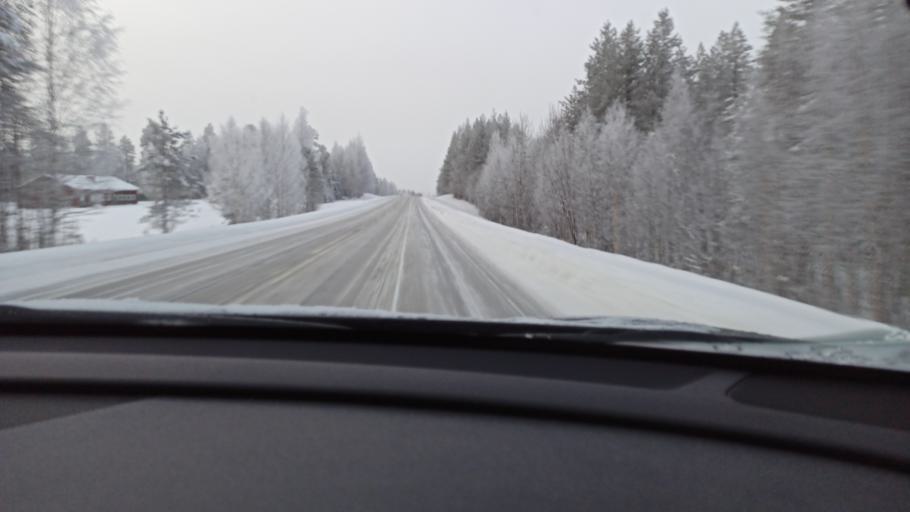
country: FI
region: Lapland
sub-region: Pohjois-Lappi
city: Sodankylae
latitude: 66.9348
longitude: 26.2694
